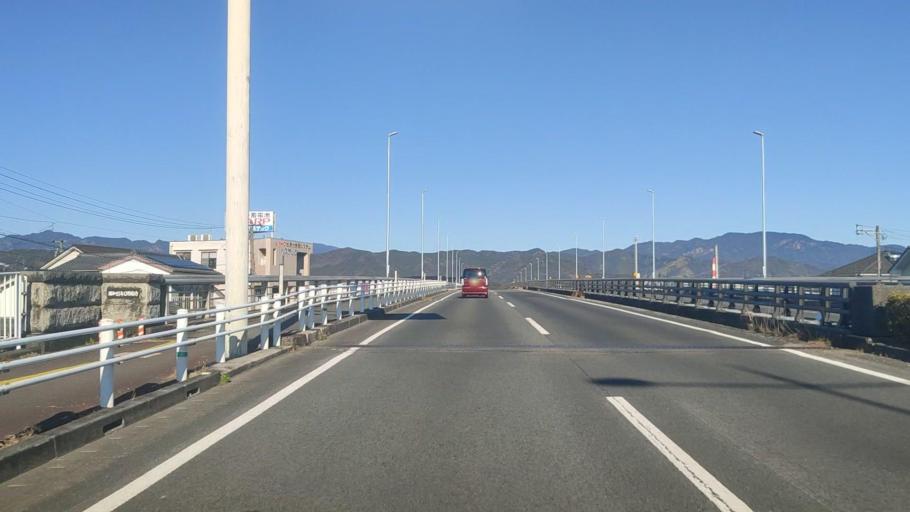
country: JP
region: Miyazaki
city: Nobeoka
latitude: 32.5810
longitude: 131.6813
